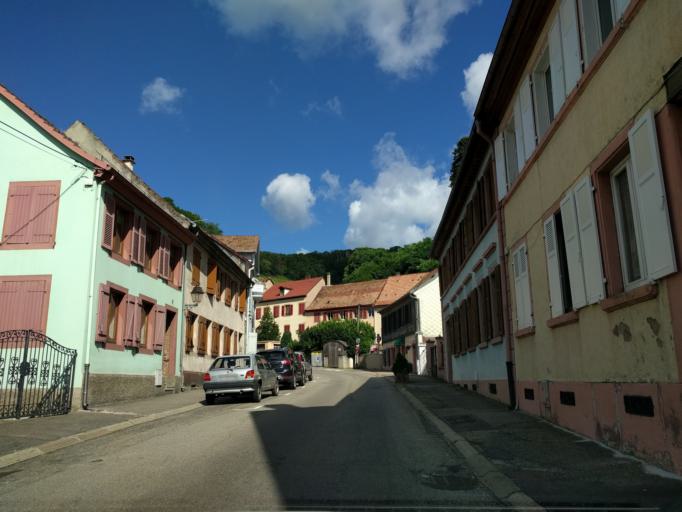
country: FR
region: Alsace
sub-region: Departement du Haut-Rhin
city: Sainte-Marie-aux-Mines
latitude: 48.2486
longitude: 7.1860
